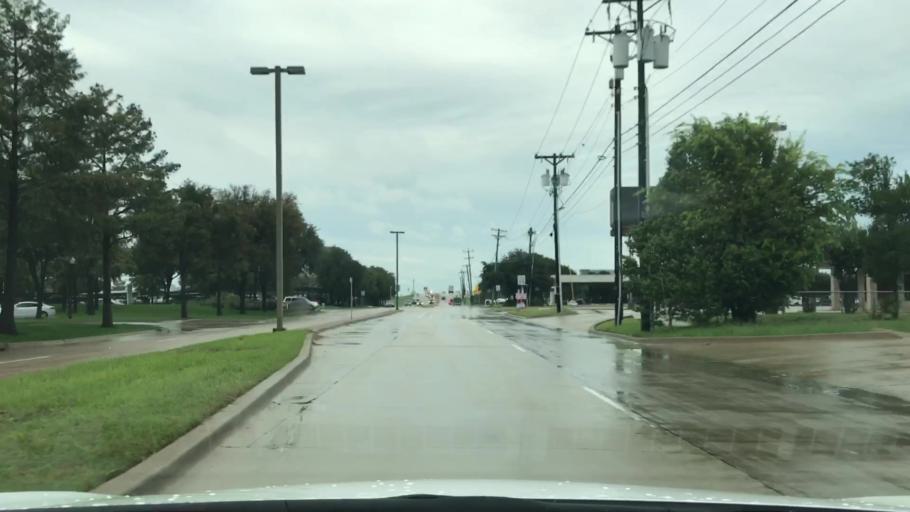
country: US
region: Texas
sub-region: Dallas County
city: Coppell
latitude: 32.9110
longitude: -97.0080
